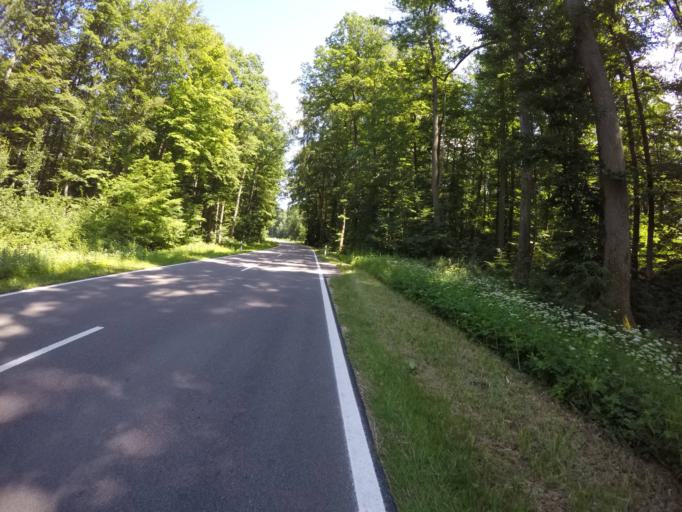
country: DE
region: Bavaria
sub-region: Lower Bavaria
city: Essing
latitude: 48.9086
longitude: 11.7839
